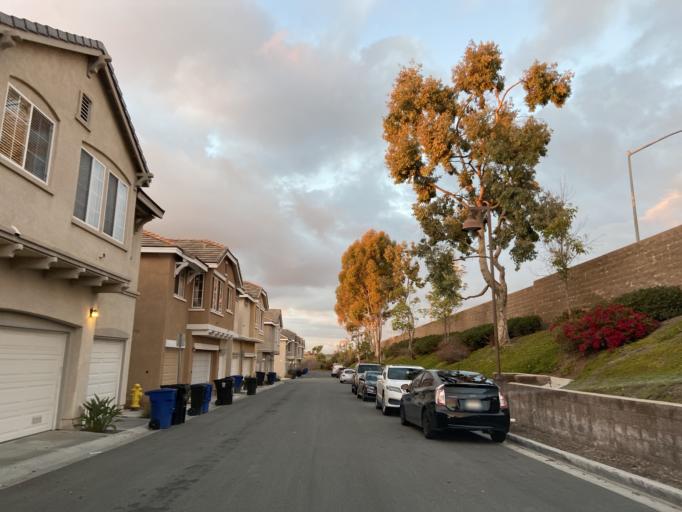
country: US
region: California
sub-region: San Diego County
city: Bonita
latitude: 32.6268
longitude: -116.9718
